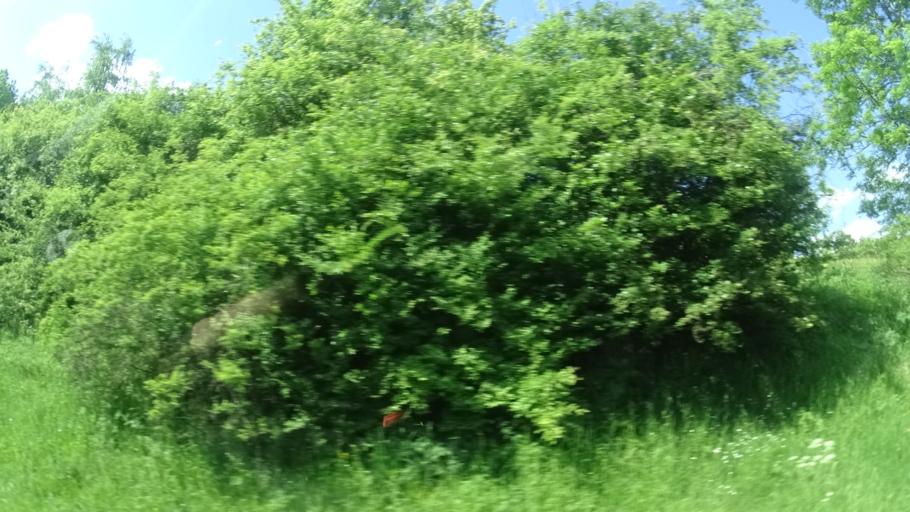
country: DE
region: Thuringia
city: Andenhausen
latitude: 50.6687
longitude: 10.0761
